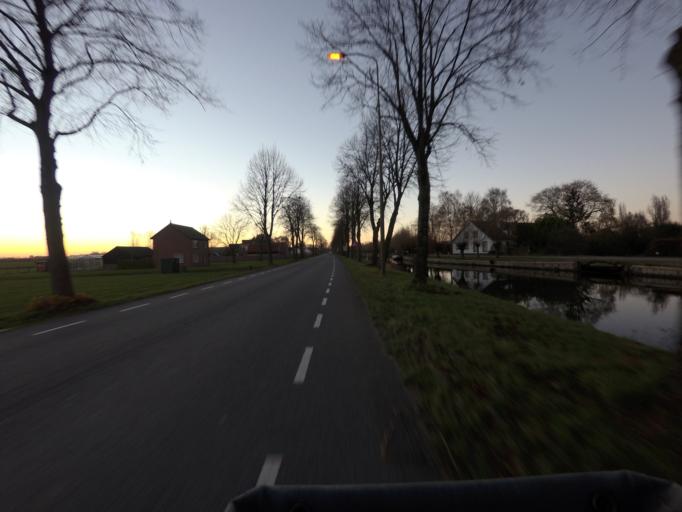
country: NL
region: Utrecht
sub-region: Stichtse Vecht
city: Spechtenkamp
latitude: 52.0902
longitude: 4.9946
